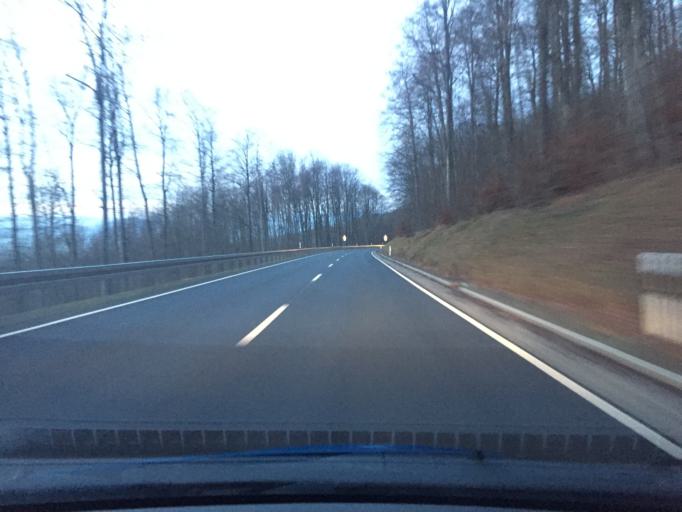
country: DE
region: Lower Saxony
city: Luerdissen
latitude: 51.9643
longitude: 9.6423
